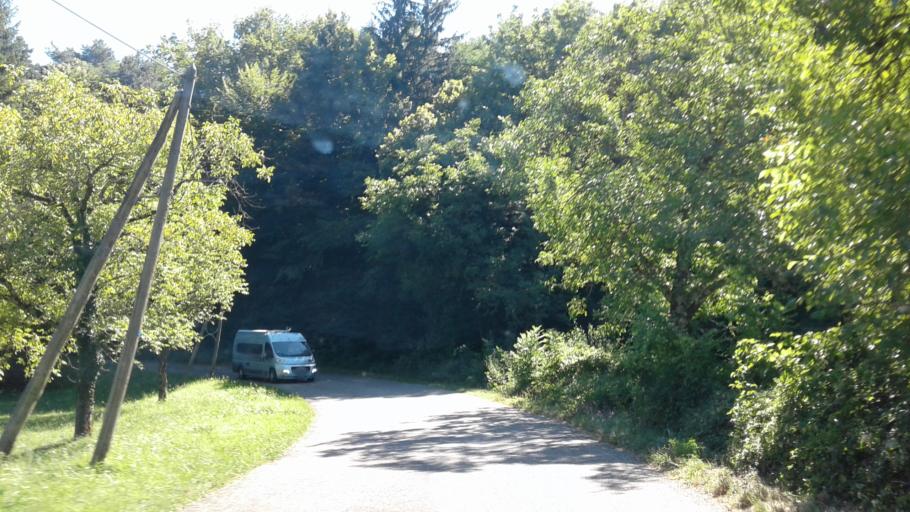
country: FR
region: Rhone-Alpes
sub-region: Departement de l'Ain
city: Artemare
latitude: 45.8766
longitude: 5.6756
